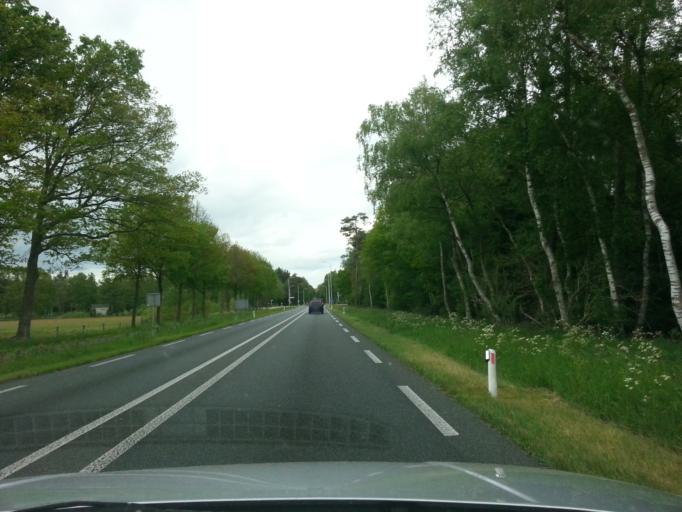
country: NL
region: Gelderland
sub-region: Gemeente Lochem
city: Almen
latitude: 52.1415
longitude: 6.3262
